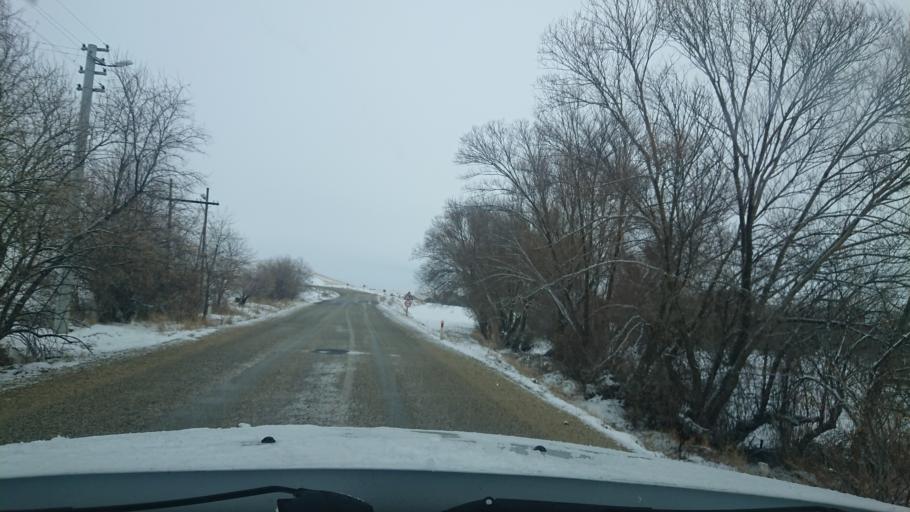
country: TR
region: Aksaray
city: Agacoren
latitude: 38.7604
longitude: 33.8695
